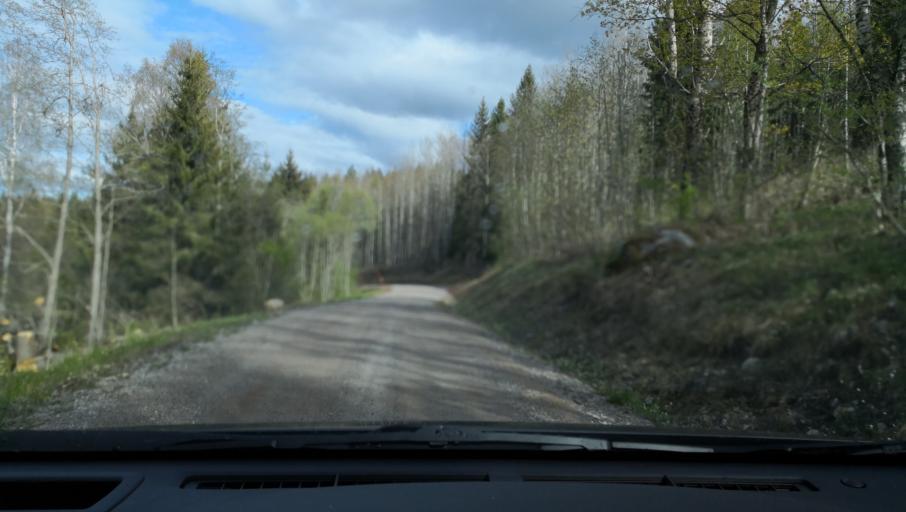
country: SE
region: Vaestmanland
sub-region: Fagersta Kommun
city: Fagersta
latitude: 60.1555
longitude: 15.6890
